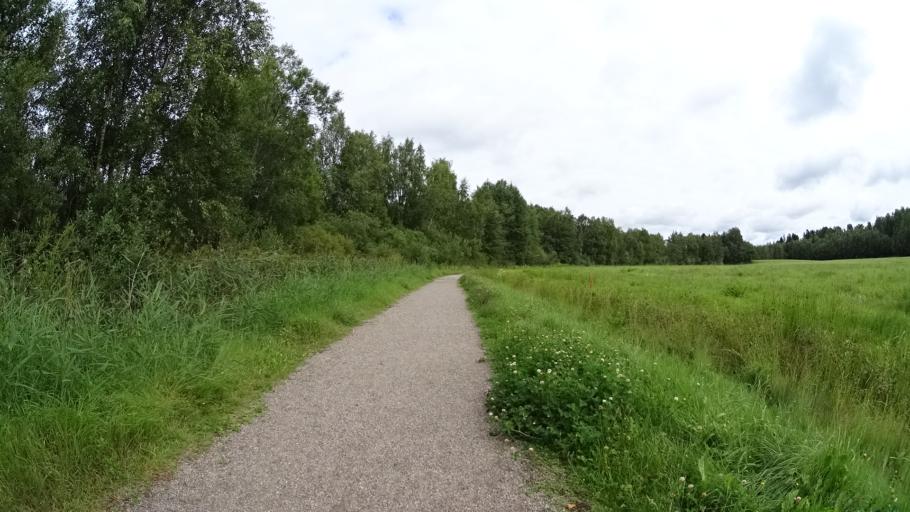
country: FI
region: Uusimaa
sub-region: Helsinki
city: Teekkarikylae
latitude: 60.2712
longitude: 24.8622
